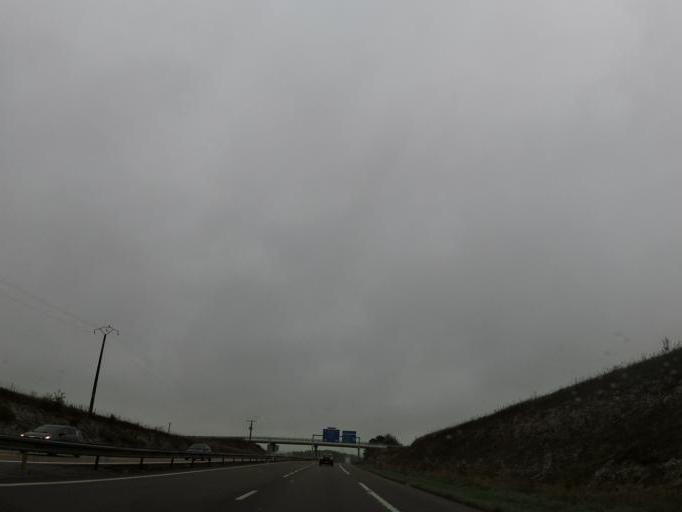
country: FR
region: Champagne-Ardenne
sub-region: Departement de la Marne
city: Fagnieres
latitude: 49.0505
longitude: 4.2961
